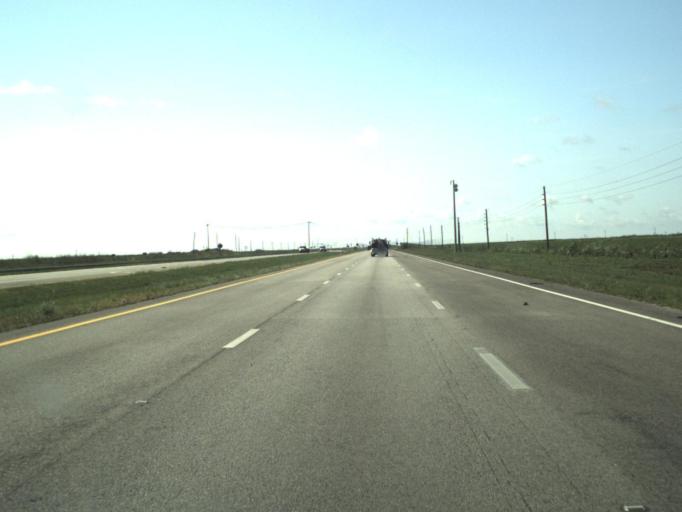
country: US
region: Florida
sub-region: Palm Beach County
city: Belle Glade Camp
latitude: 26.3755
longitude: -80.5695
